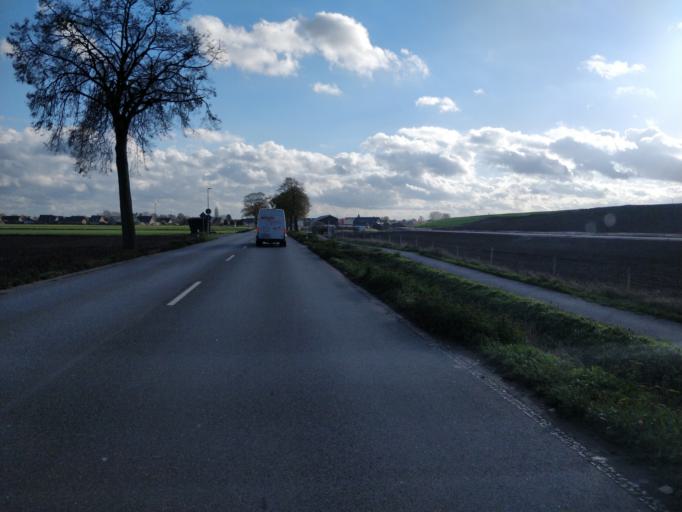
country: DE
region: North Rhine-Westphalia
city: Rees
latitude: 51.8090
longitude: 6.3655
